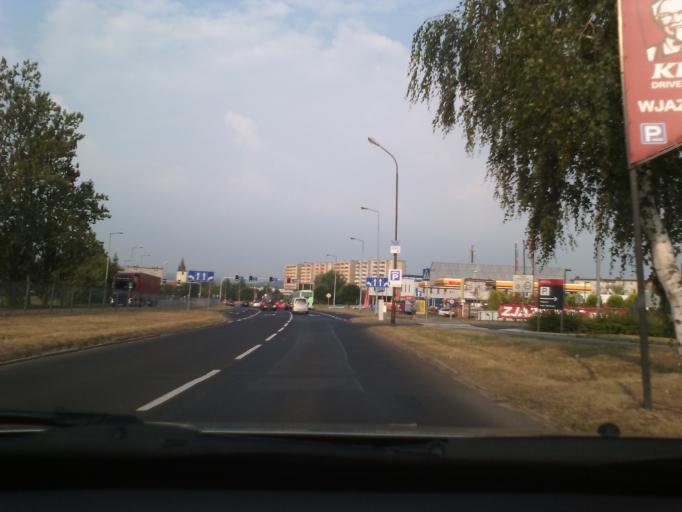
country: PL
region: Lower Silesian Voivodeship
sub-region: Powiat jeleniogorski
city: Jezow Sudecki
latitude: 50.9204
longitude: 15.7609
